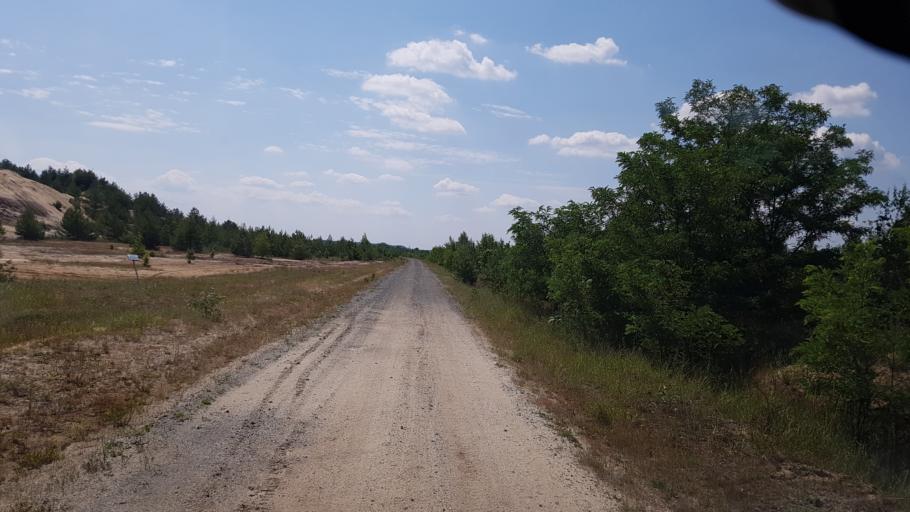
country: DE
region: Brandenburg
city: Sallgast
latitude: 51.5690
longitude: 13.8050
